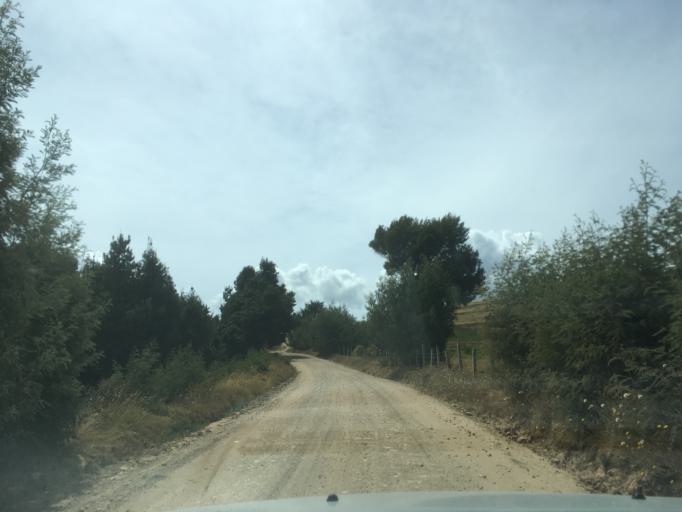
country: CO
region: Boyaca
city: Aquitania
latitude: 5.5620
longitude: -72.9528
